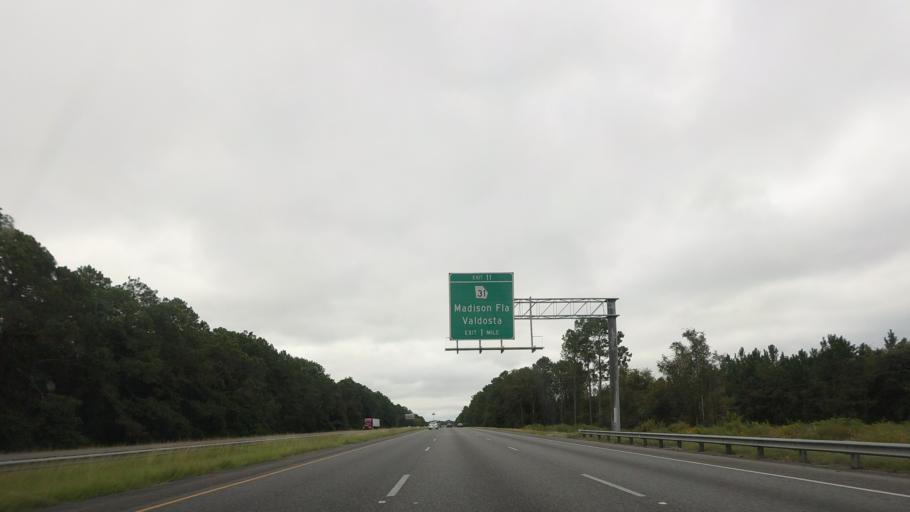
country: US
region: Georgia
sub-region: Lowndes County
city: Valdosta
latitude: 30.7647
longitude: -83.2854
